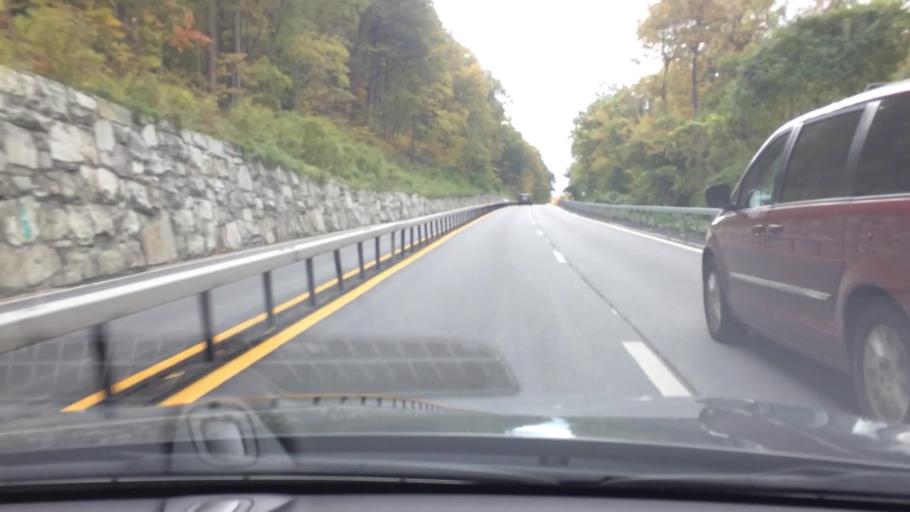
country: US
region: New York
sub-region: Dutchess County
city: Hillside Lake
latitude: 41.5294
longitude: -73.7750
